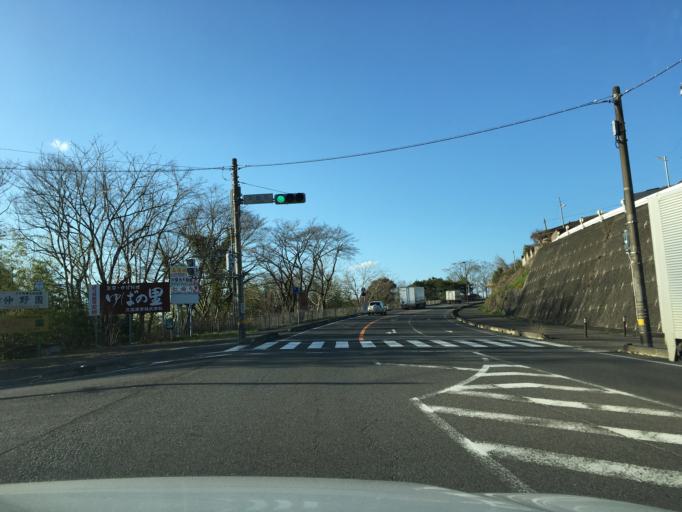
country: JP
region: Ibaraki
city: Daigo
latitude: 36.7623
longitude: 140.3590
